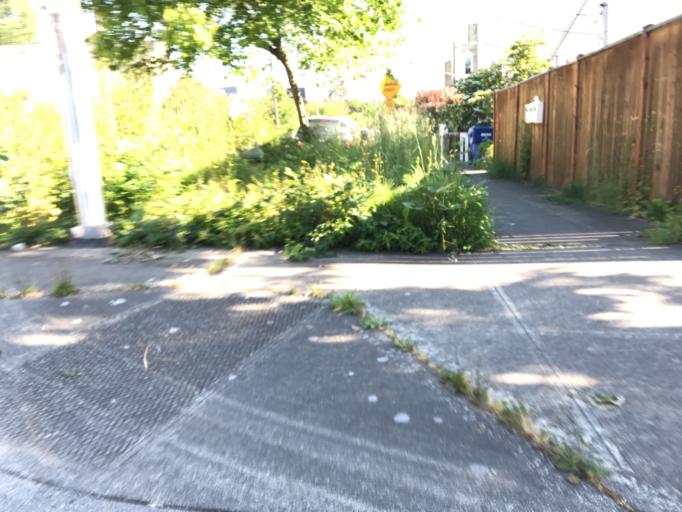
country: US
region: Washington
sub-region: King County
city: Seattle
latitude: 47.5884
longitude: -122.3105
